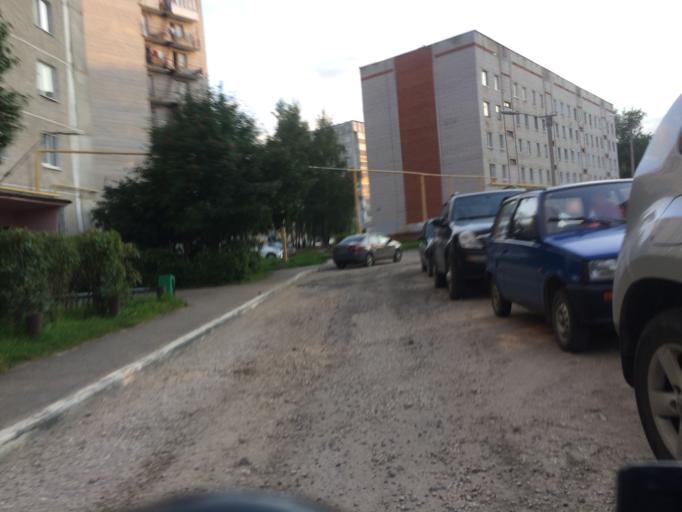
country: RU
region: Mariy-El
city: Yoshkar-Ola
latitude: 56.6432
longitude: 47.8508
